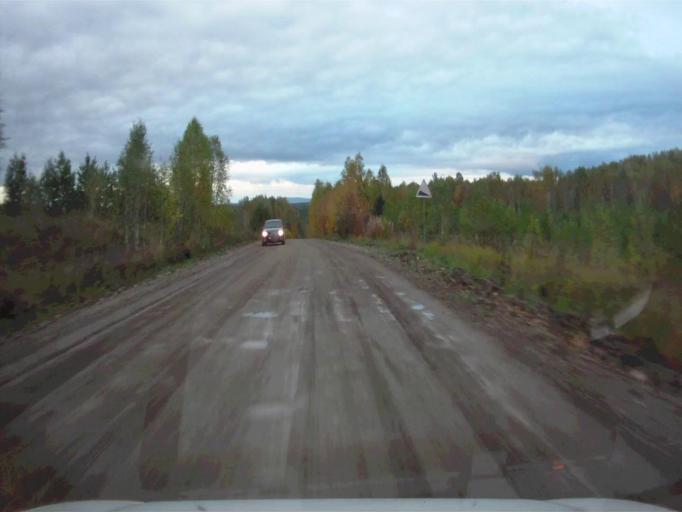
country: RU
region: Sverdlovsk
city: Mikhaylovsk
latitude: 56.2097
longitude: 59.2104
